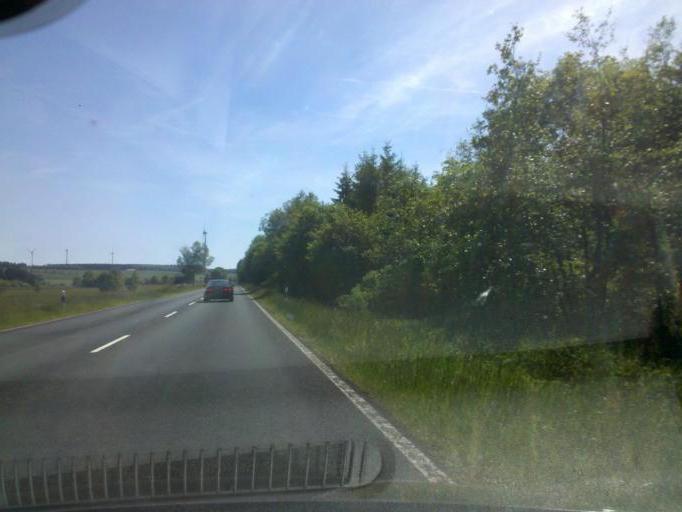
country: DE
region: Rheinland-Pfalz
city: Rehe
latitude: 50.6678
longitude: 8.1352
